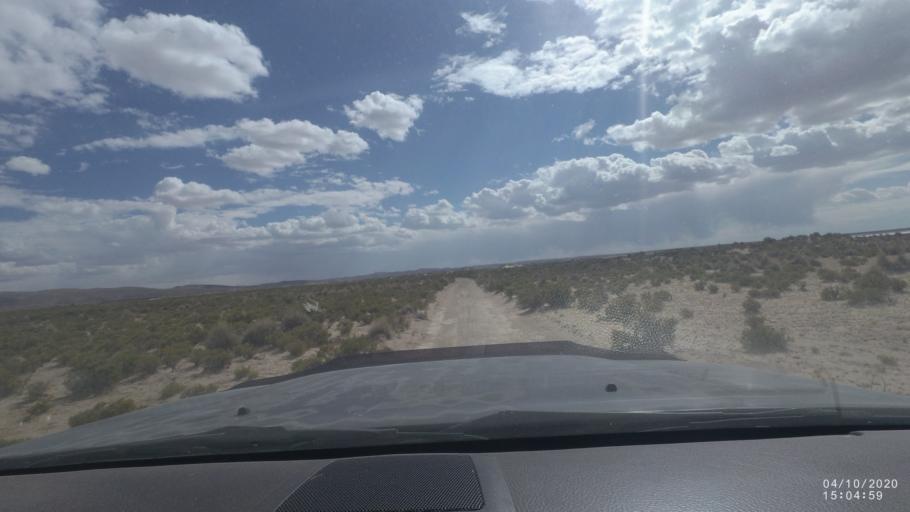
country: BO
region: Oruro
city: Poopo
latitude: -18.6912
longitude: -67.5534
